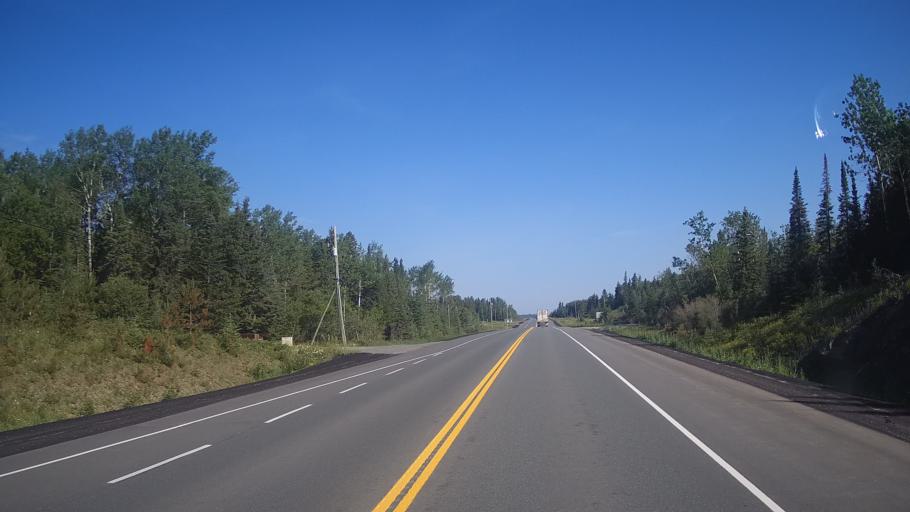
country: CA
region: Ontario
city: Dryden
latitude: 49.6560
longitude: -92.4778
